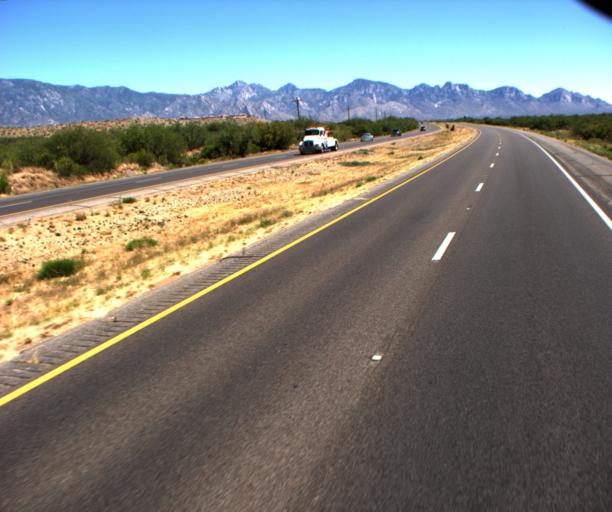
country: US
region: Arizona
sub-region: Pima County
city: Catalina
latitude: 32.5385
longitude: -110.9310
